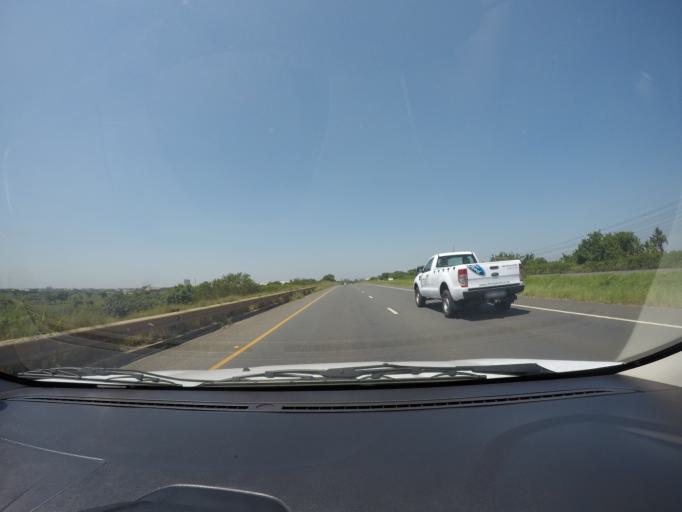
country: ZA
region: KwaZulu-Natal
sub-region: uThungulu District Municipality
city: Richards Bay
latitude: -28.7762
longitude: 32.0062
